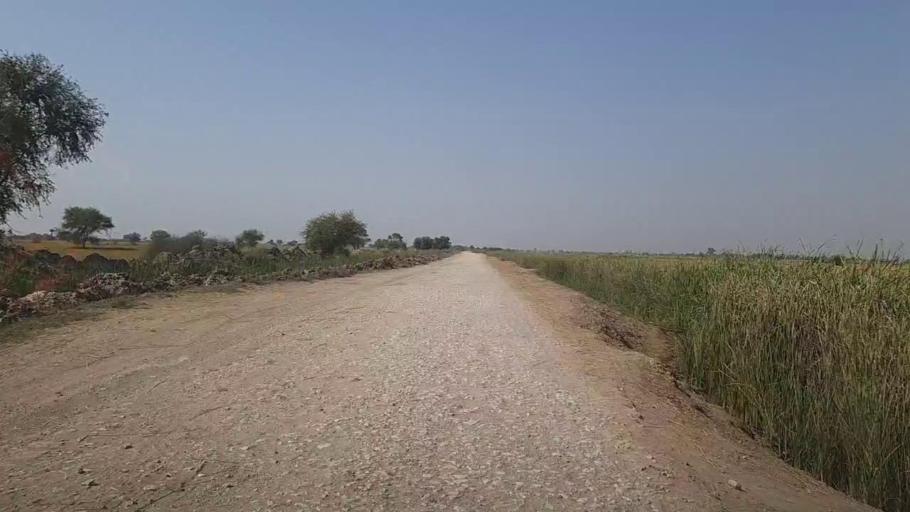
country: PK
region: Sindh
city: Kandhkot
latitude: 28.3962
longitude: 69.2721
